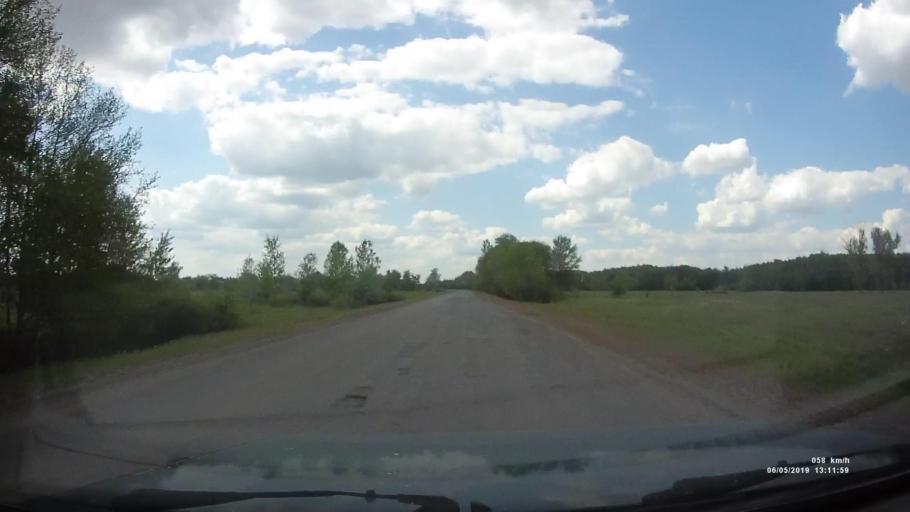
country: RU
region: Rostov
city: Ust'-Donetskiy
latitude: 47.7545
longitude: 40.9528
